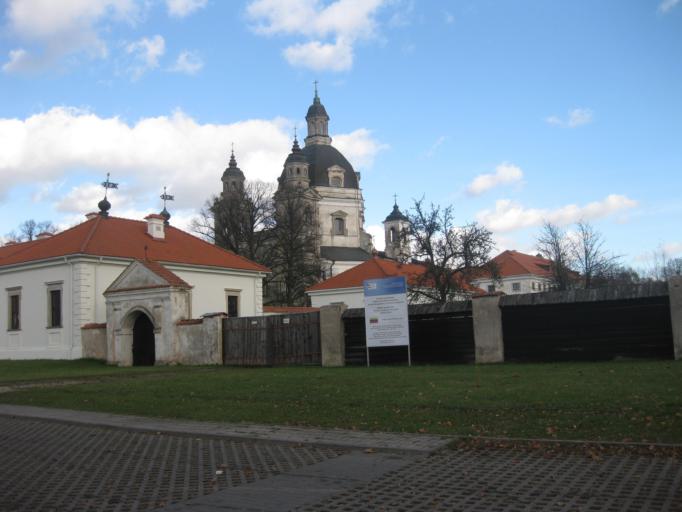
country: LT
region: Kauno apskritis
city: Dainava (Kaunas)
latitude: 54.8760
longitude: 24.0206
